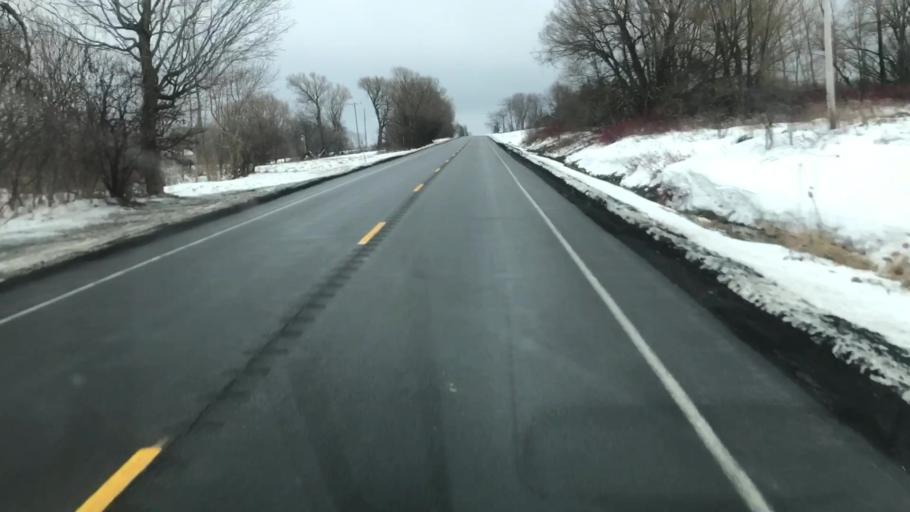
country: US
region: New York
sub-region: Cayuga County
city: Moravia
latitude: 42.7786
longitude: -76.3390
